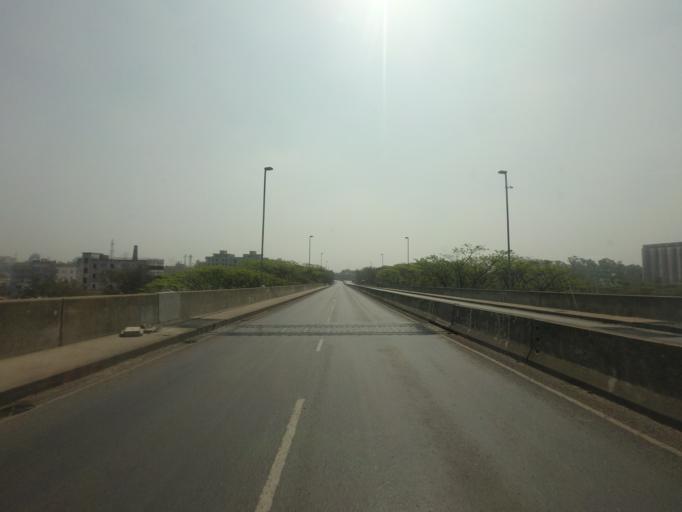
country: BD
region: Dhaka
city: Bhairab Bazar
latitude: 24.0417
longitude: 90.9988
